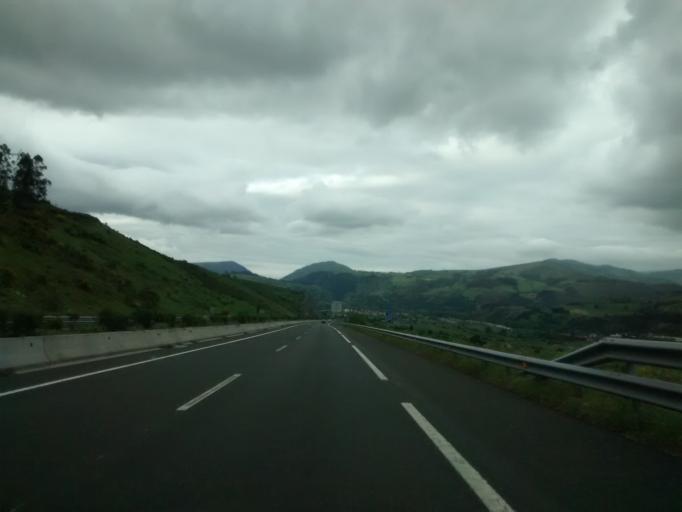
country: ES
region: Cantabria
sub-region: Provincia de Cantabria
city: Molledo
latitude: 43.1567
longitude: -4.0530
